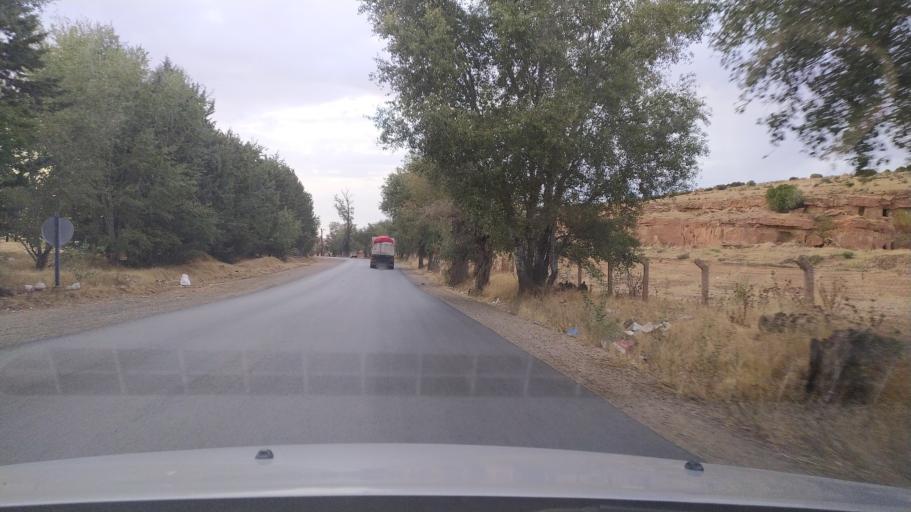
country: DZ
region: Tiaret
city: Frenda
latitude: 35.0477
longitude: 1.0812
